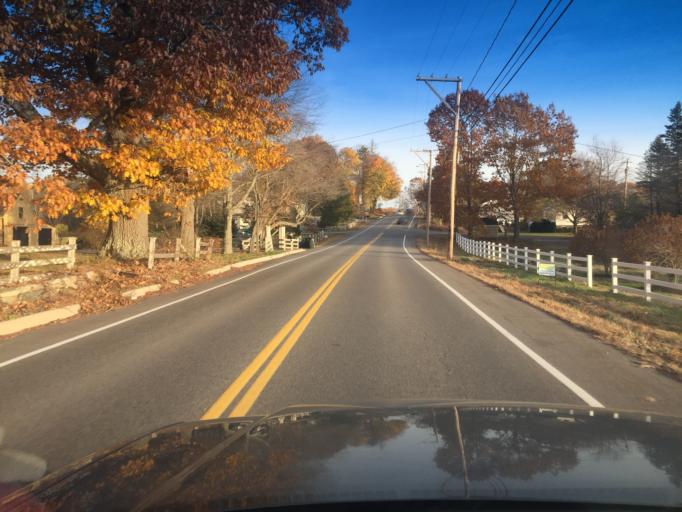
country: US
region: Maine
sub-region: York County
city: York Harbor
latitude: 43.1601
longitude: -70.7027
